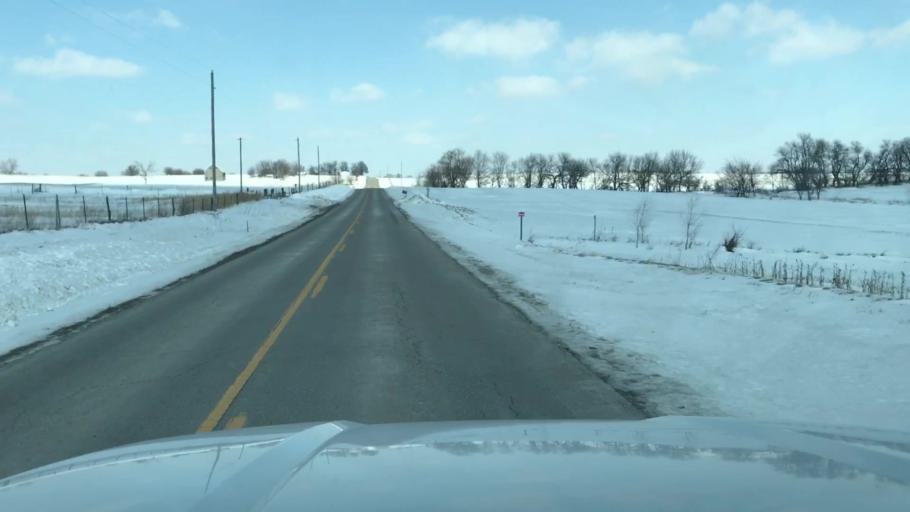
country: US
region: Missouri
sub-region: Nodaway County
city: Maryville
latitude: 40.3487
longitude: -94.7224
